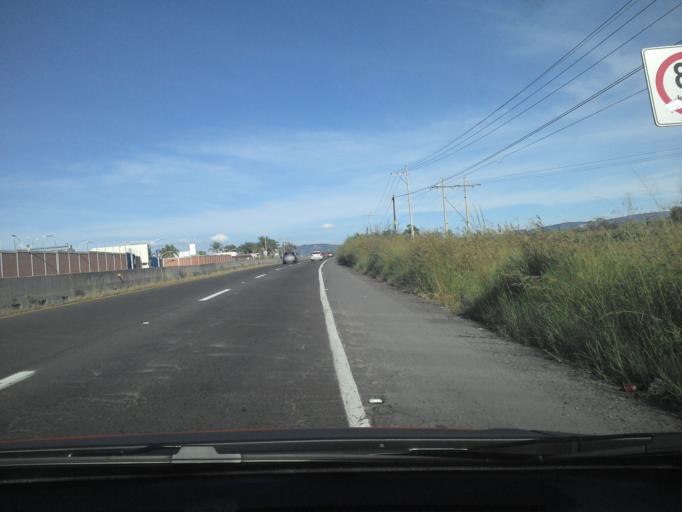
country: MX
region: Jalisco
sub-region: Tala
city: Los Ruisenores
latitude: 20.7050
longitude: -103.6849
